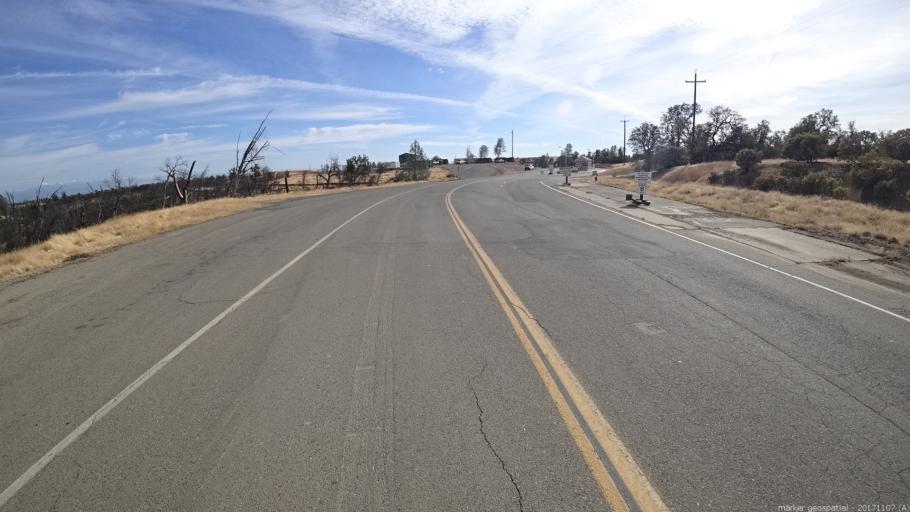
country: US
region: California
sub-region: Shasta County
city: Shasta
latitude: 40.4897
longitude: -122.5389
